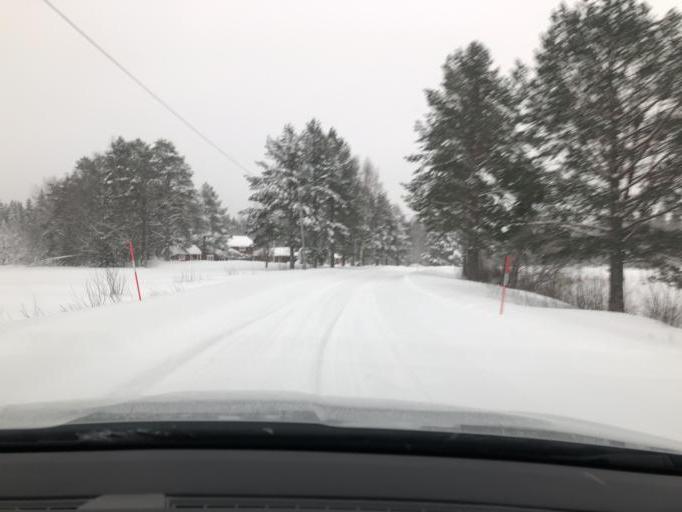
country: SE
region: Vaesterbotten
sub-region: Umea Kommun
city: Saevar
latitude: 63.9445
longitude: 20.7079
